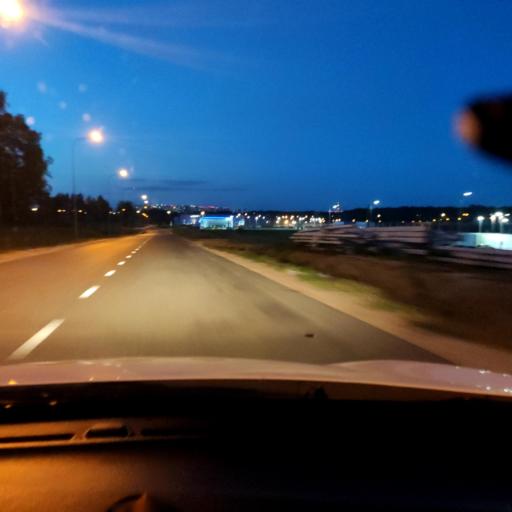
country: RU
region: Tatarstan
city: Osinovo
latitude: 55.8508
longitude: 48.8354
